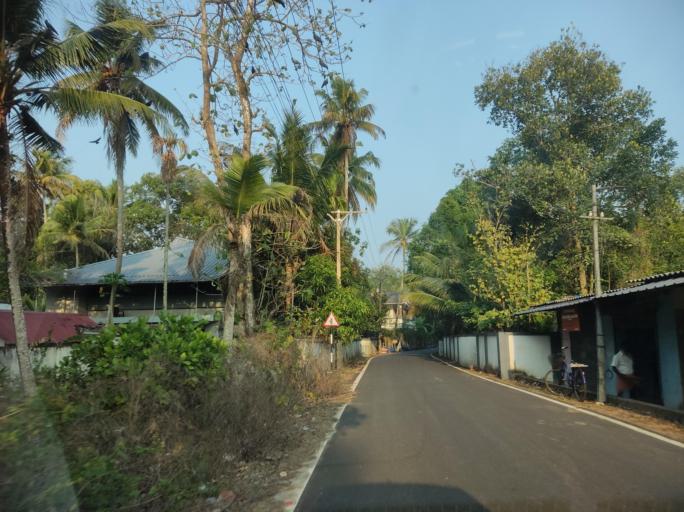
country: IN
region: Kerala
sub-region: Alappuzha
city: Shertallai
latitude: 9.6154
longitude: 76.3150
